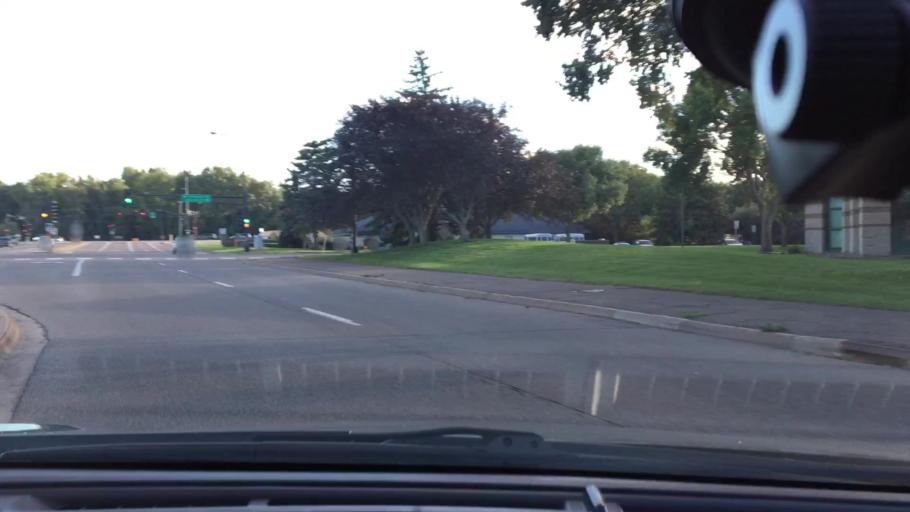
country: US
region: Minnesota
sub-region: Hennepin County
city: Plymouth
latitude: 44.9865
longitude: -93.4108
